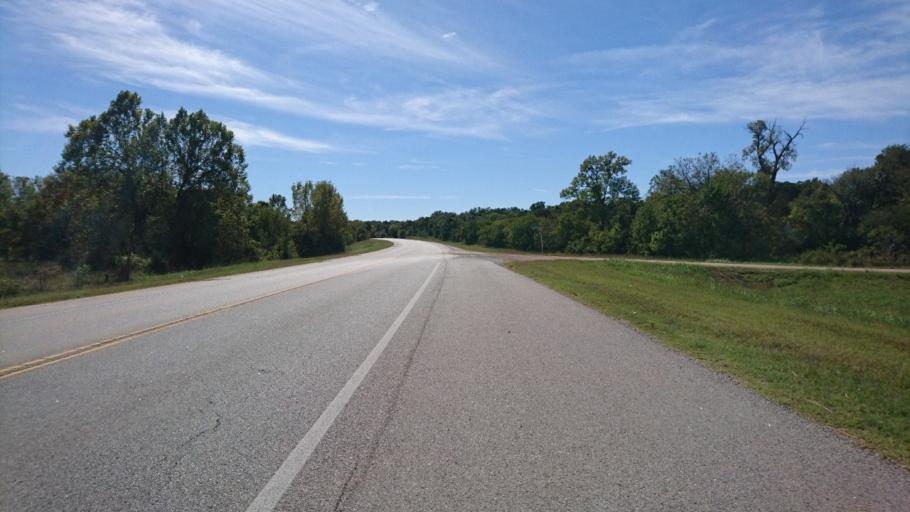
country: US
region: Oklahoma
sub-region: Lincoln County
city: Stroud
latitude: 35.7369
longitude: -96.7189
